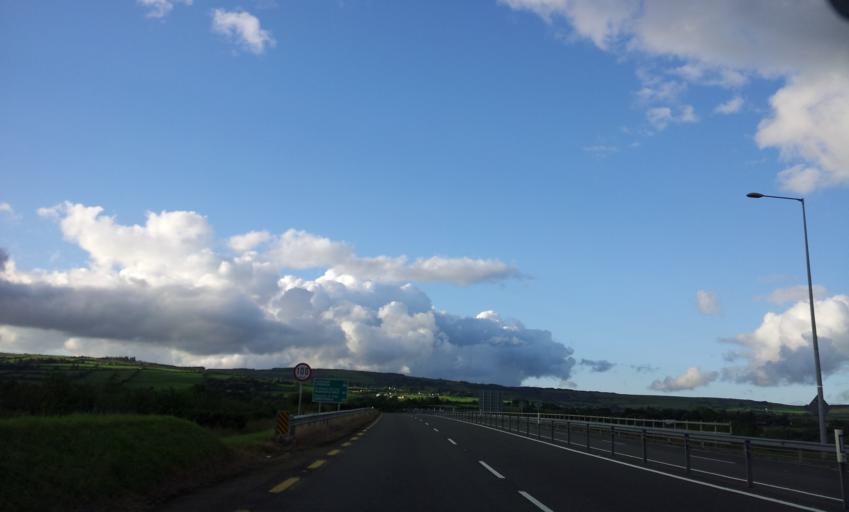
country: IE
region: Munster
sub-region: Ciarrai
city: Castleisland
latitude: 52.2366
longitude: -9.4862
